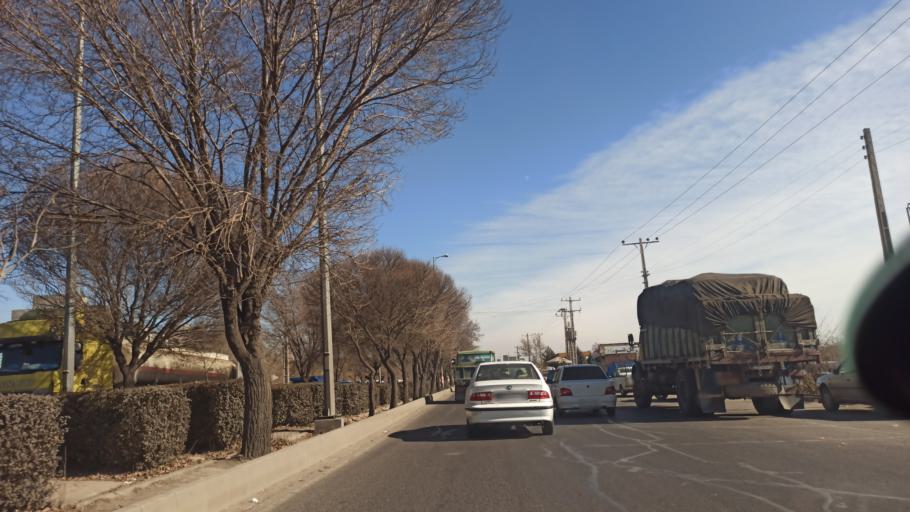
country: IR
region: Qazvin
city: Qazvin
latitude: 36.2580
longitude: 49.9887
